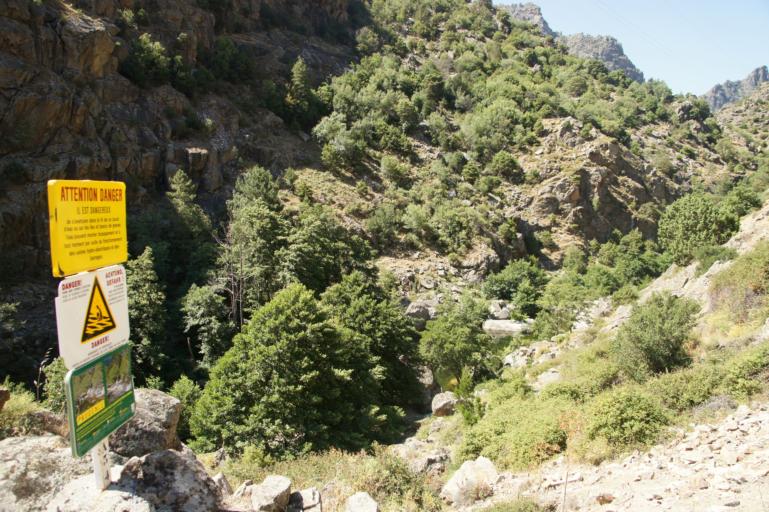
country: FR
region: Corsica
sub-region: Departement de la Haute-Corse
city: Corte
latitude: 42.3746
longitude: 9.0829
